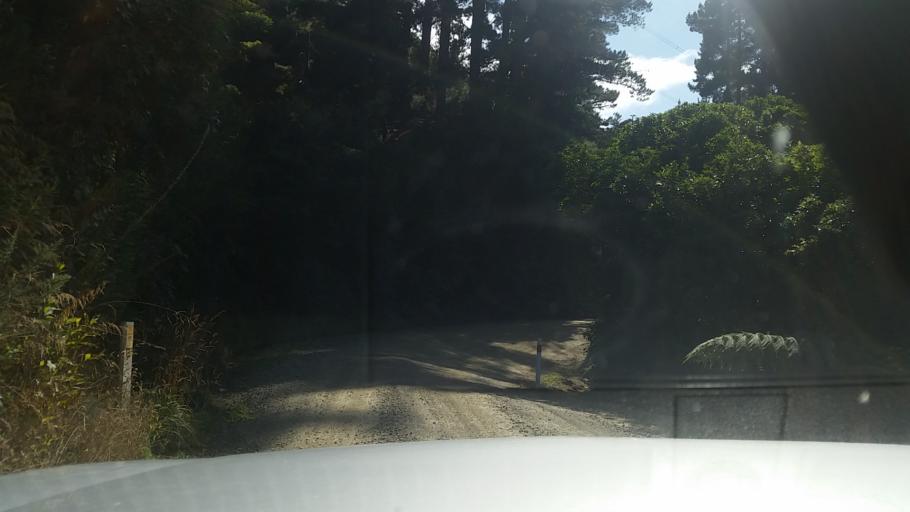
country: NZ
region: Marlborough
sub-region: Marlborough District
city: Picton
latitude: -41.2882
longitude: 174.1735
